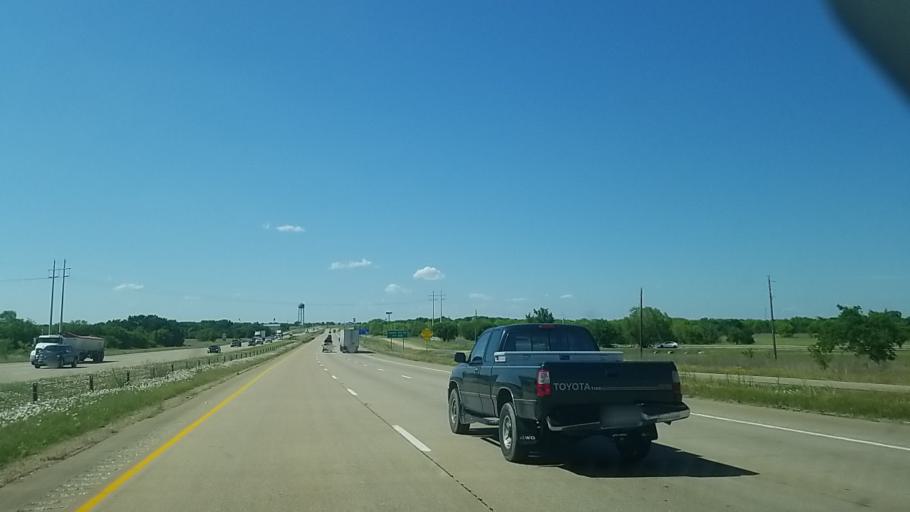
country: US
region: Texas
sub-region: Ellis County
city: Palmer
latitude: 32.4025
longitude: -96.6559
